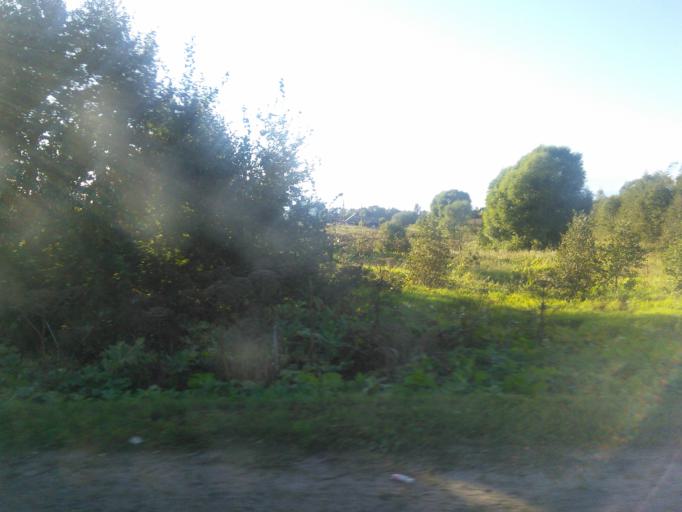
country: RU
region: Jaroslavl
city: Poshekhon'ye
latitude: 58.4259
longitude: 38.9969
